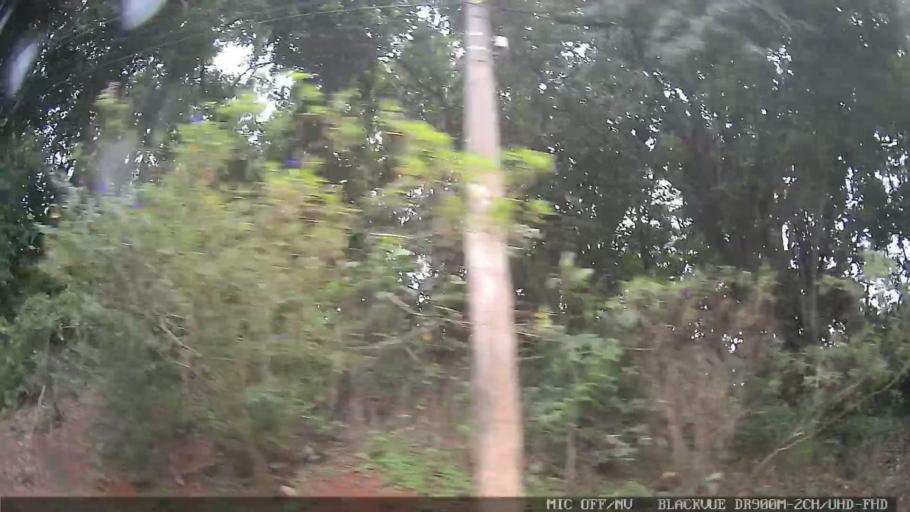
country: BR
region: Sao Paulo
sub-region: Pedreira
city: Pedreira
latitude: -22.6899
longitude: -46.8803
